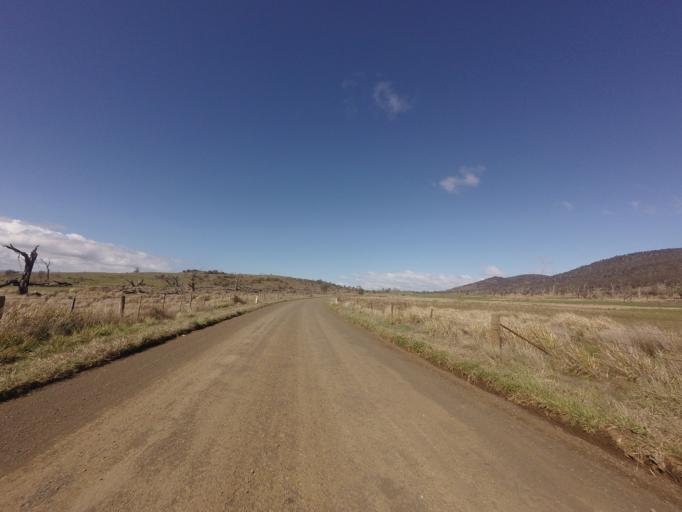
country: AU
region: Tasmania
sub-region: Northern Midlands
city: Evandale
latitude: -41.9288
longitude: 147.4142
